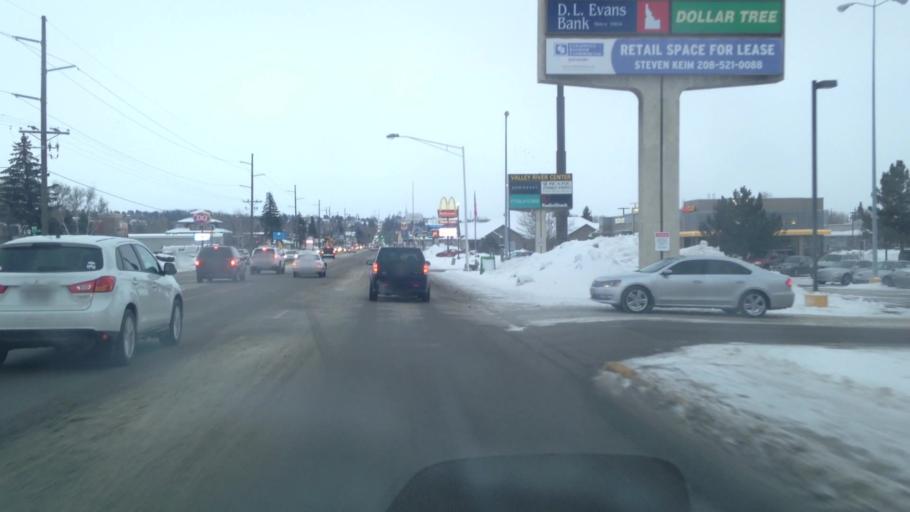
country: US
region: Idaho
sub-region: Madison County
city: Rexburg
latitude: 43.8347
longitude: -111.7782
